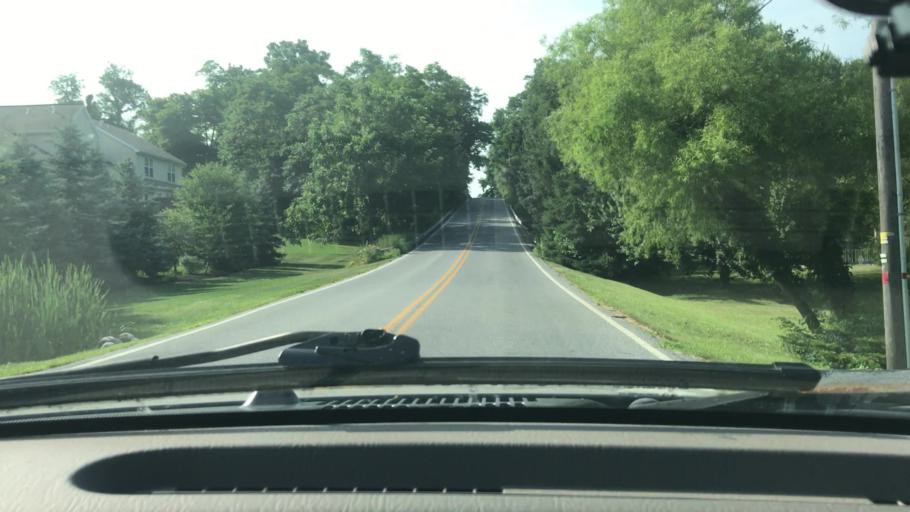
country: US
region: Pennsylvania
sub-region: Lancaster County
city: Rheems
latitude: 40.1556
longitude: -76.5749
